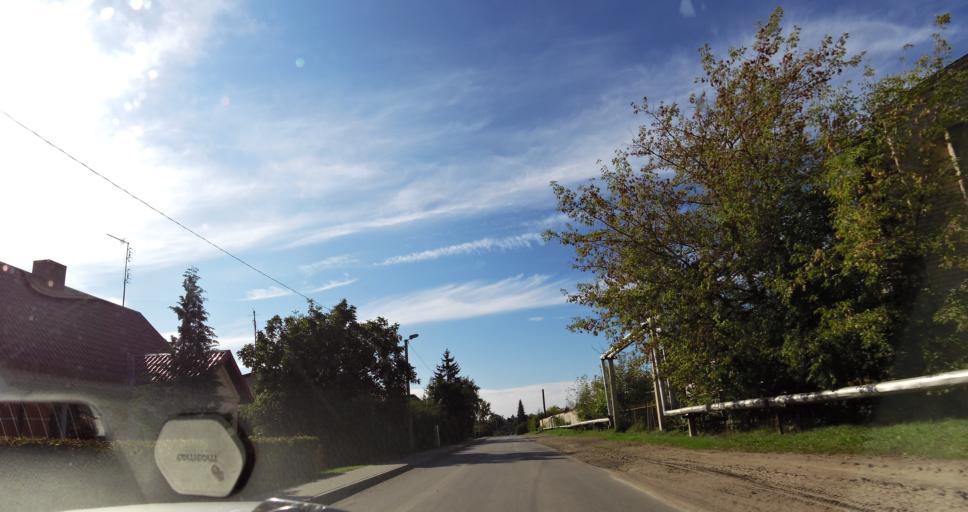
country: LT
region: Panevezys
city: Pasvalys
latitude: 56.0661
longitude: 24.3973
